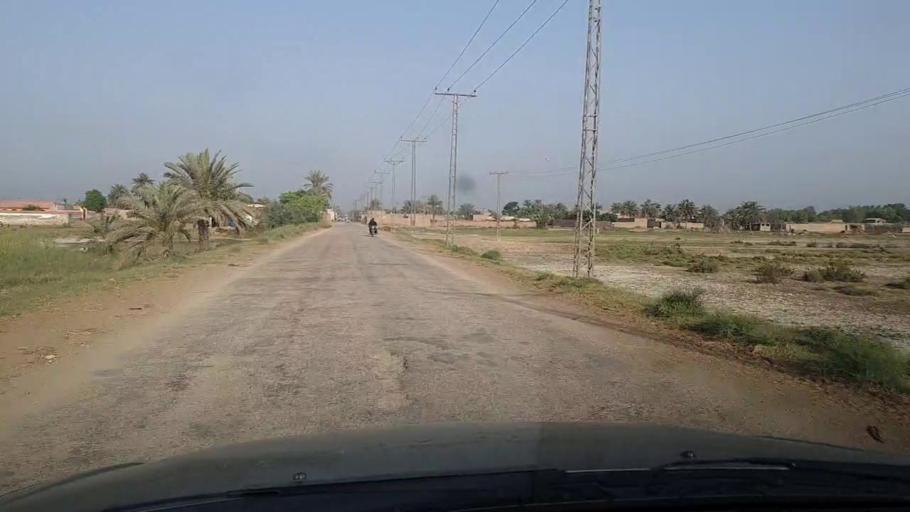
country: PK
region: Sindh
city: Pir jo Goth
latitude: 27.5699
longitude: 68.6311
